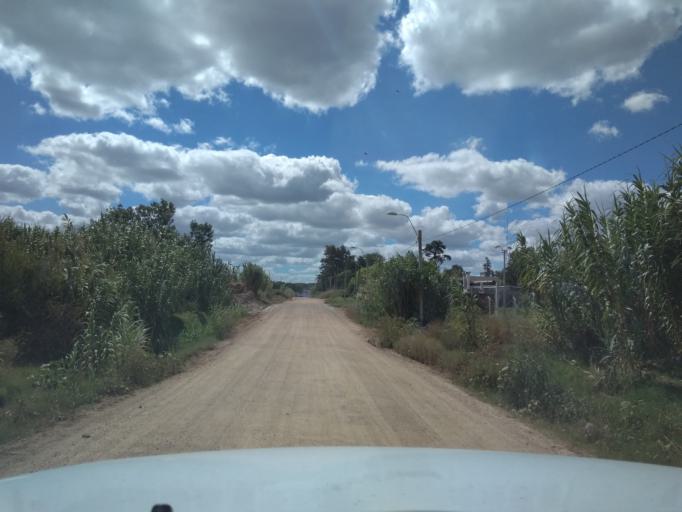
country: UY
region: Canelones
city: Colonia Nicolich
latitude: -34.8275
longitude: -55.9938
